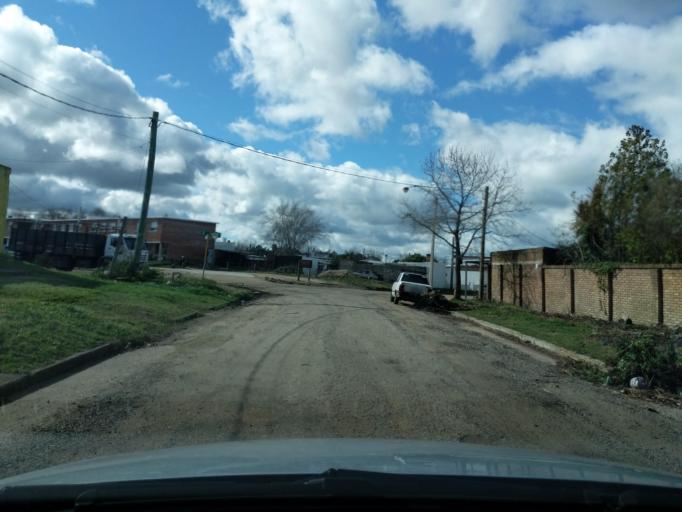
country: UY
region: Florida
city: Florida
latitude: -34.0818
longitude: -56.2252
